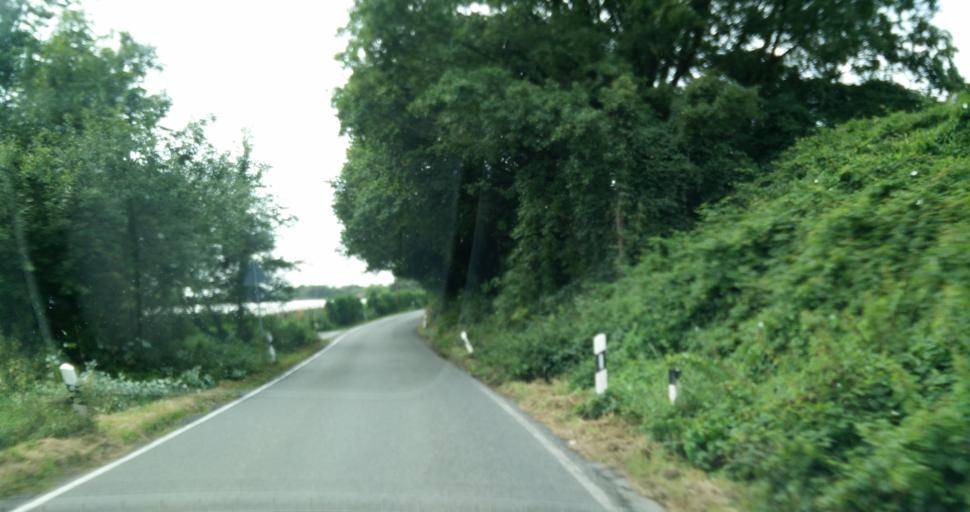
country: DE
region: North Rhine-Westphalia
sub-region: Regierungsbezirk Dusseldorf
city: Ratingen
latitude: 51.2840
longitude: 6.8787
